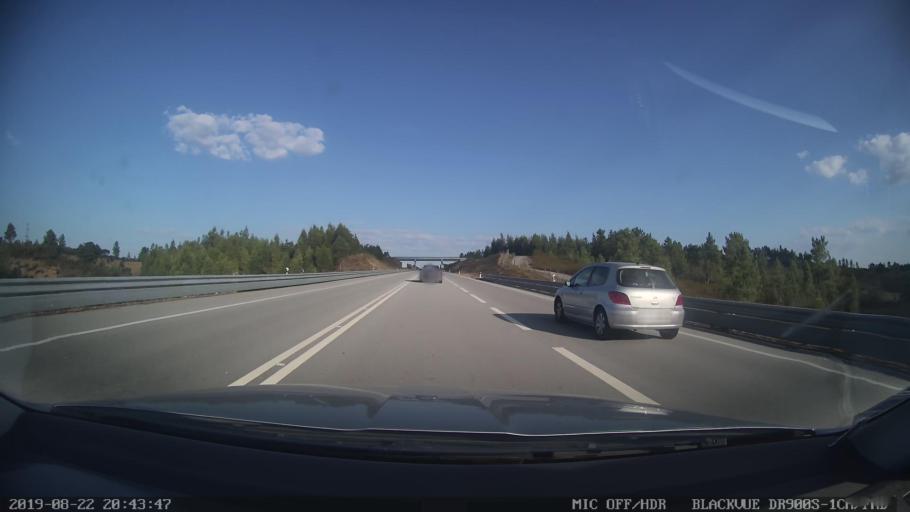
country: PT
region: Castelo Branco
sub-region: Proenca-A-Nova
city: Proenca-a-Nova
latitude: 39.7011
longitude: -7.8385
